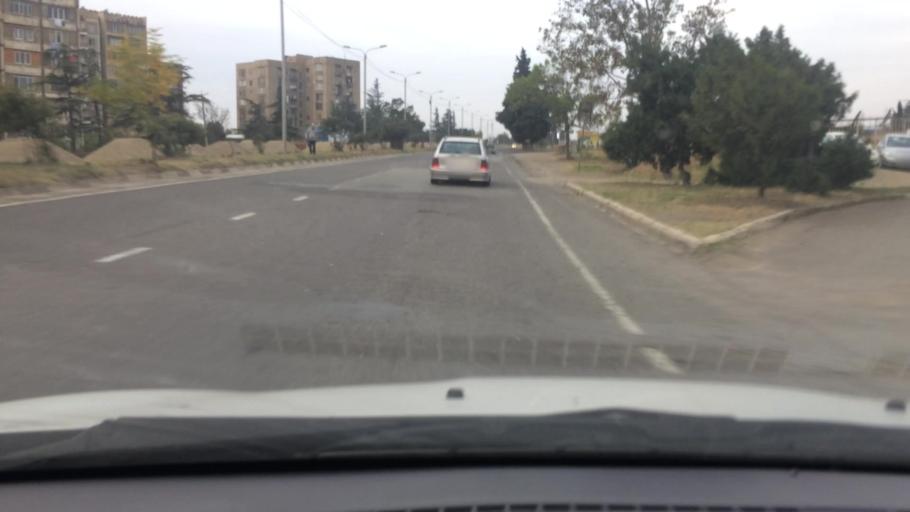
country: GE
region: T'bilisi
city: Tbilisi
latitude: 41.6457
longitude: 44.8962
